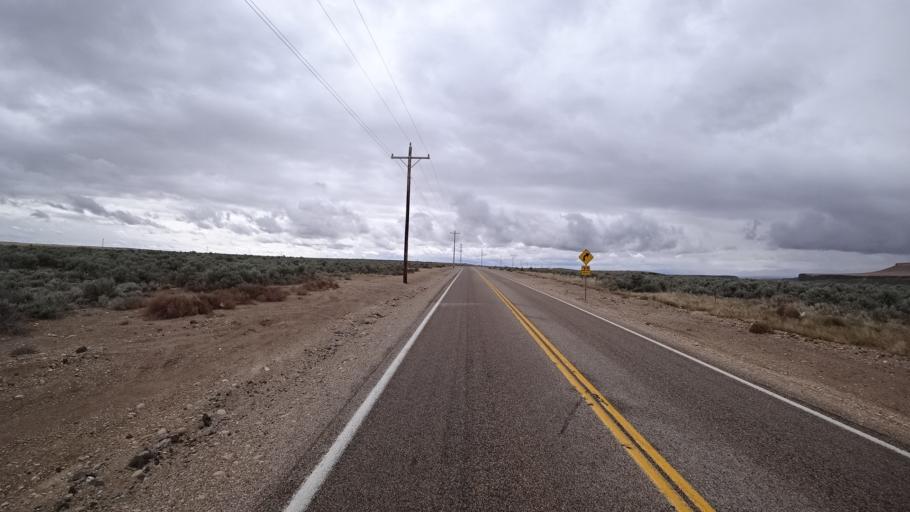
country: US
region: Idaho
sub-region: Owyhee County
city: Murphy
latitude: 43.2523
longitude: -116.3734
